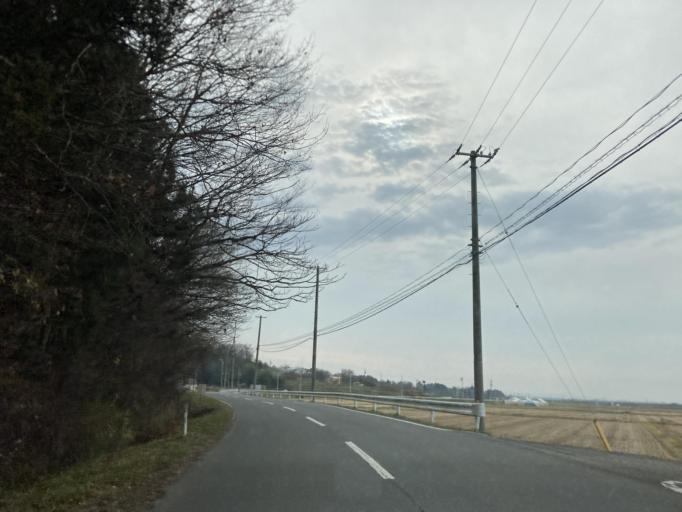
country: JP
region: Miyagi
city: Wakuya
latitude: 38.6855
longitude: 141.2749
